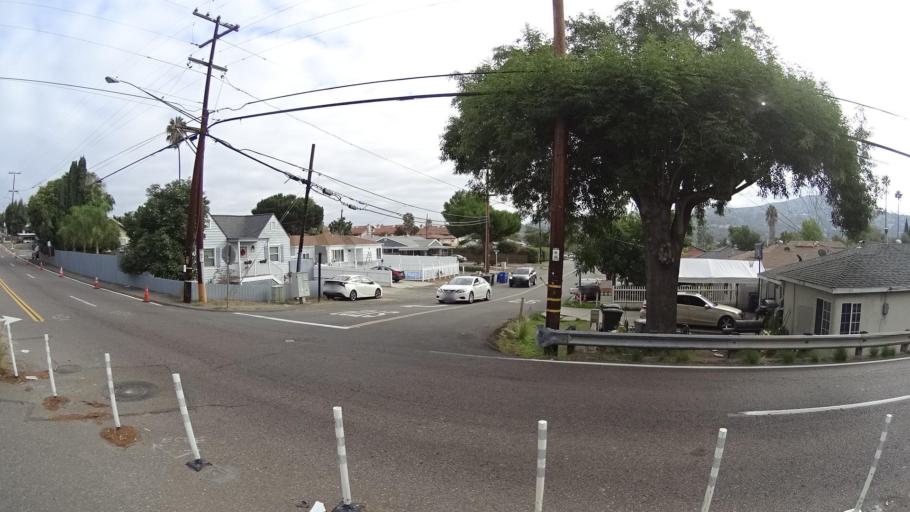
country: US
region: California
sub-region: San Diego County
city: Lemon Grove
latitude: 32.7346
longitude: -117.0146
